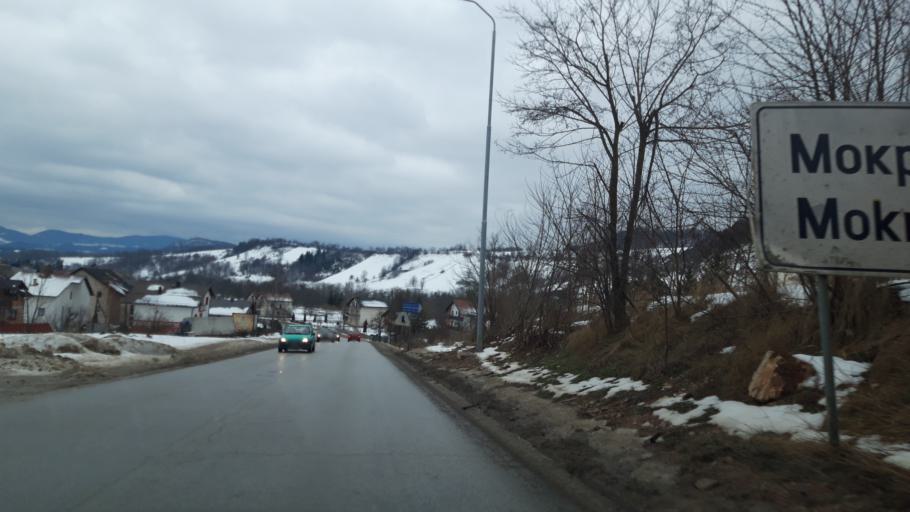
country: BA
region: Republika Srpska
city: Pale
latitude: 43.8872
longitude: 18.6132
